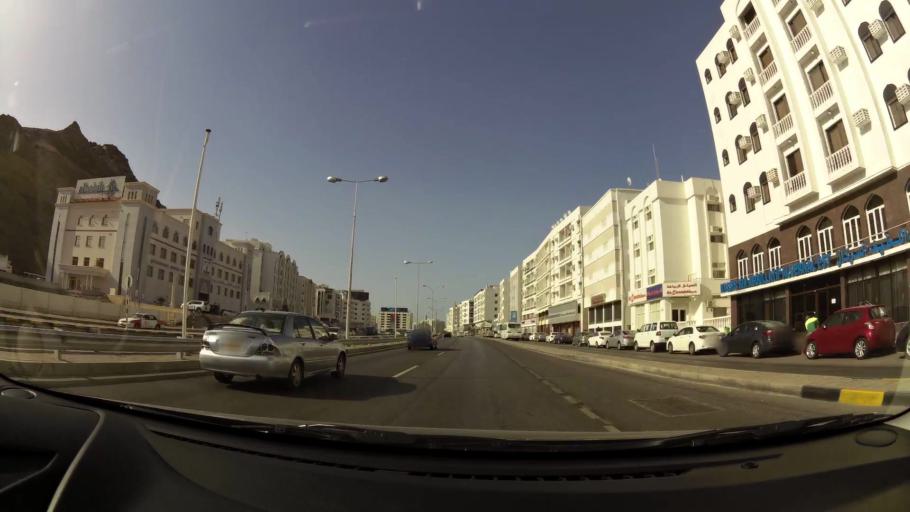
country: OM
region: Muhafazat Masqat
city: Muscat
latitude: 23.5892
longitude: 58.5414
